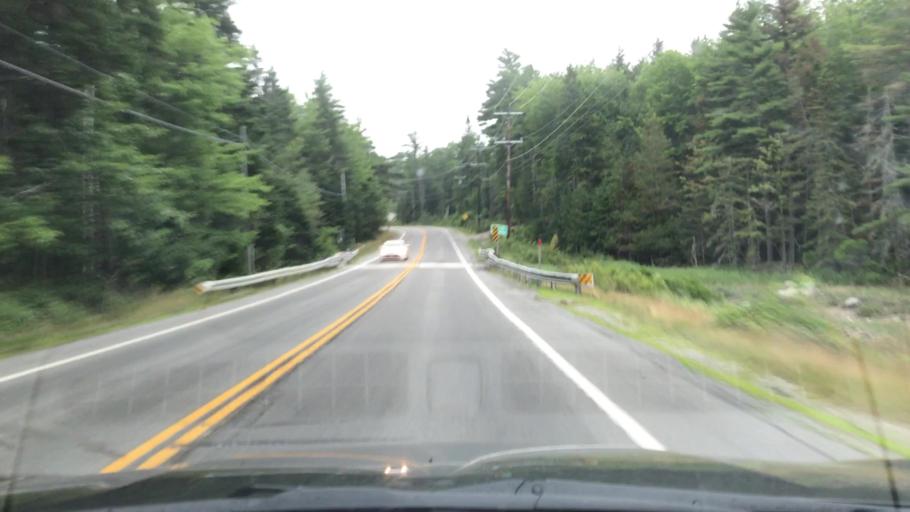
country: US
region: Maine
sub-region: Hancock County
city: Trenton
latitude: 44.3771
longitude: -68.3312
